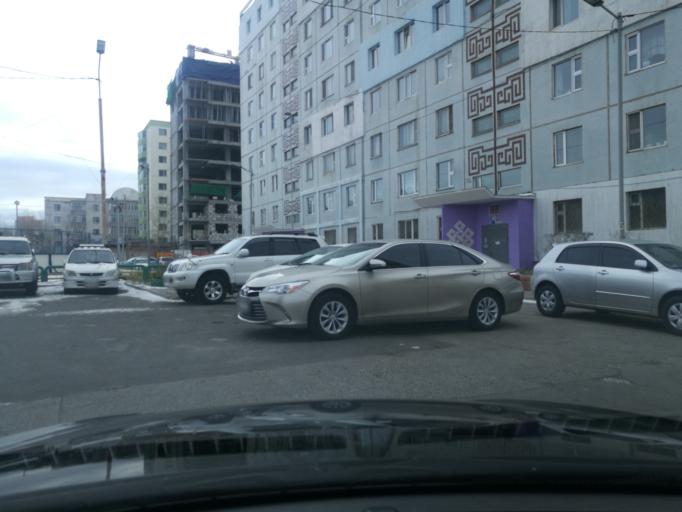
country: MN
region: Ulaanbaatar
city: Ulaanbaatar
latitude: 47.9098
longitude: 106.8965
